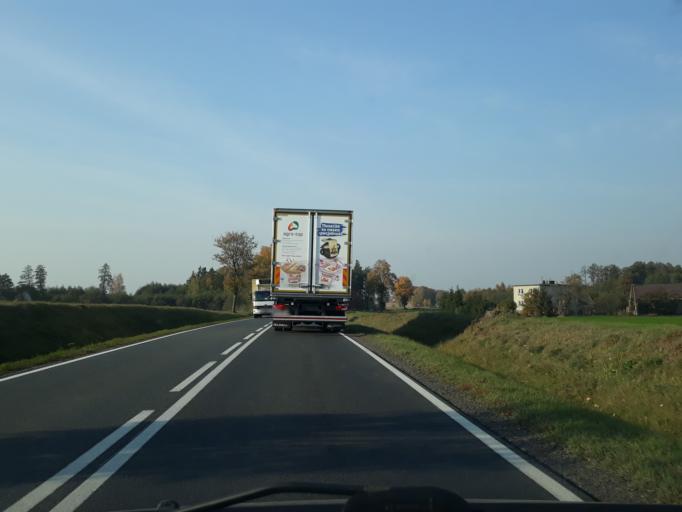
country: PL
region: Kujawsko-Pomorskie
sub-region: Powiat sepolenski
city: Sepolno Krajenskie
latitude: 53.4889
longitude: 17.5147
